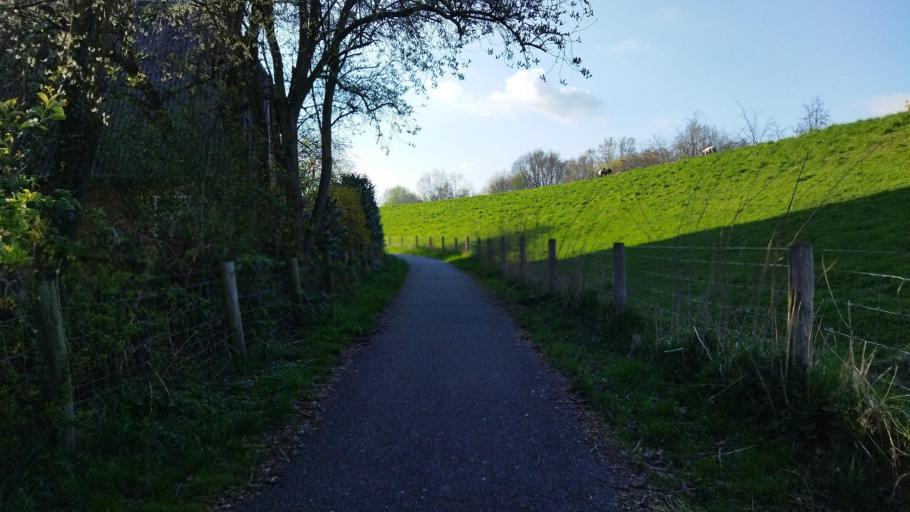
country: DE
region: Lower Saxony
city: Neuenkirchen
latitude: 53.1801
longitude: 8.5479
